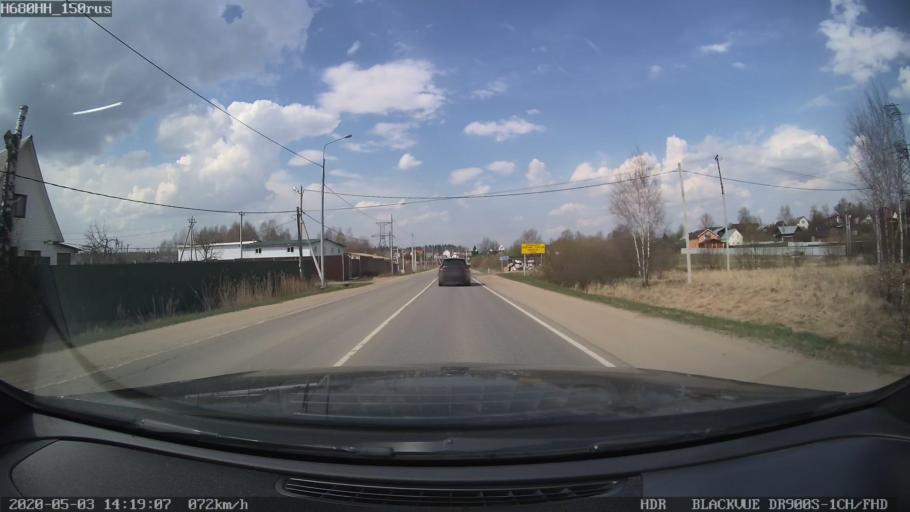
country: RU
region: Moskovskaya
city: Solnechnogorsk
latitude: 56.2286
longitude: 36.9683
